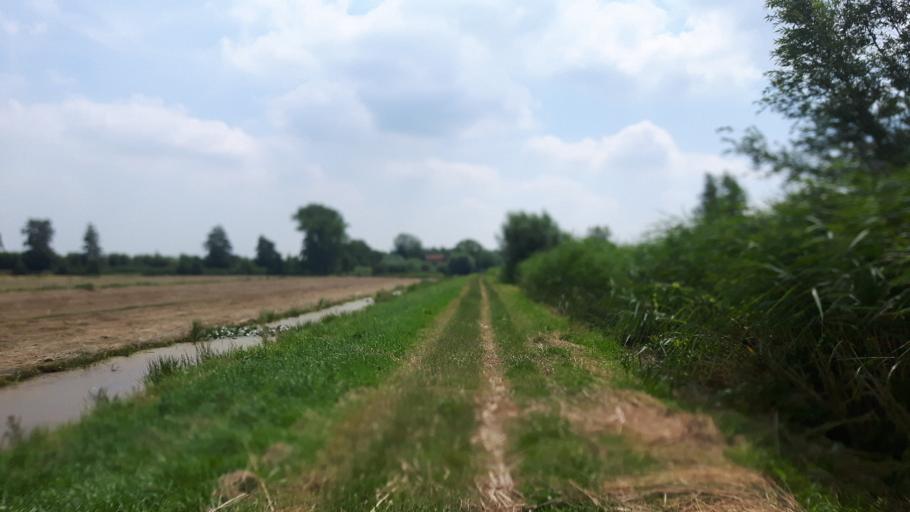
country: NL
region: Utrecht
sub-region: Gemeente Lopik
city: Lopik
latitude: 51.9461
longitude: 4.9964
